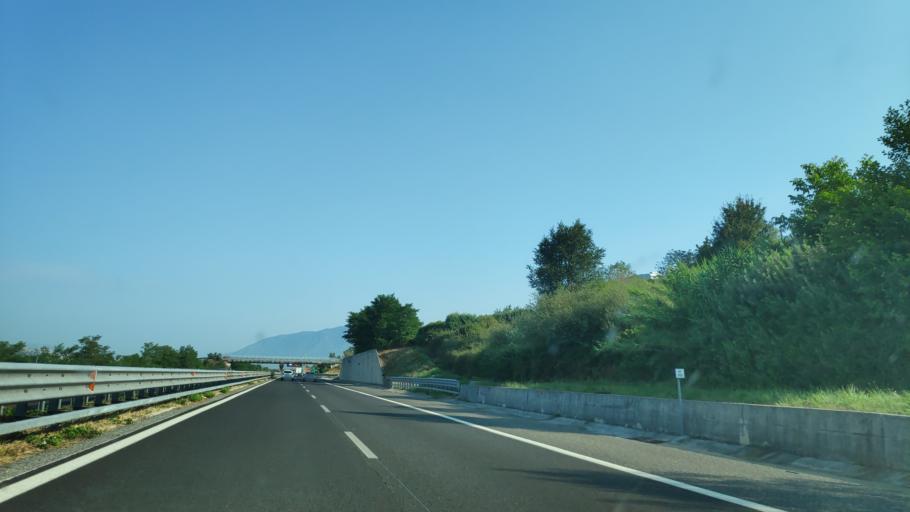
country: IT
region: Campania
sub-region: Provincia di Salerno
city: Buonabitacolo
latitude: 40.2791
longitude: 15.6535
